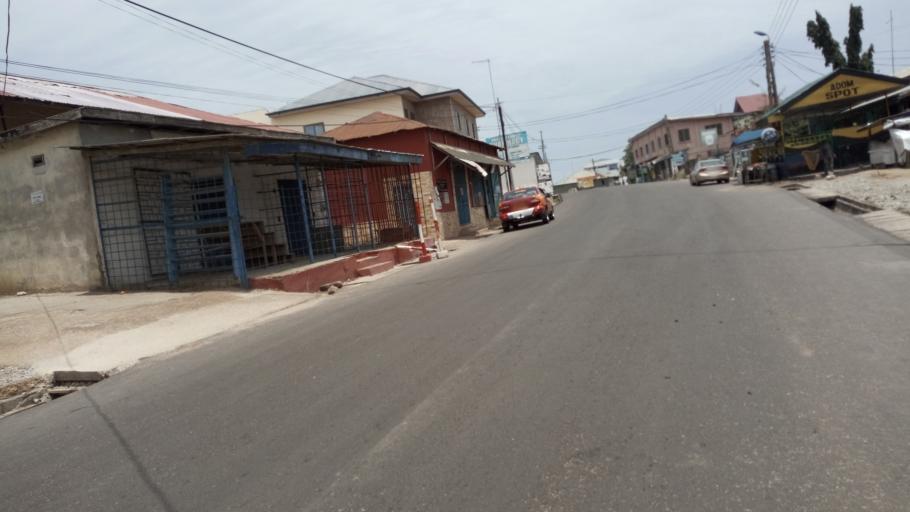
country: GH
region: Central
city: Winneba
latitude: 5.3418
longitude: -0.6254
